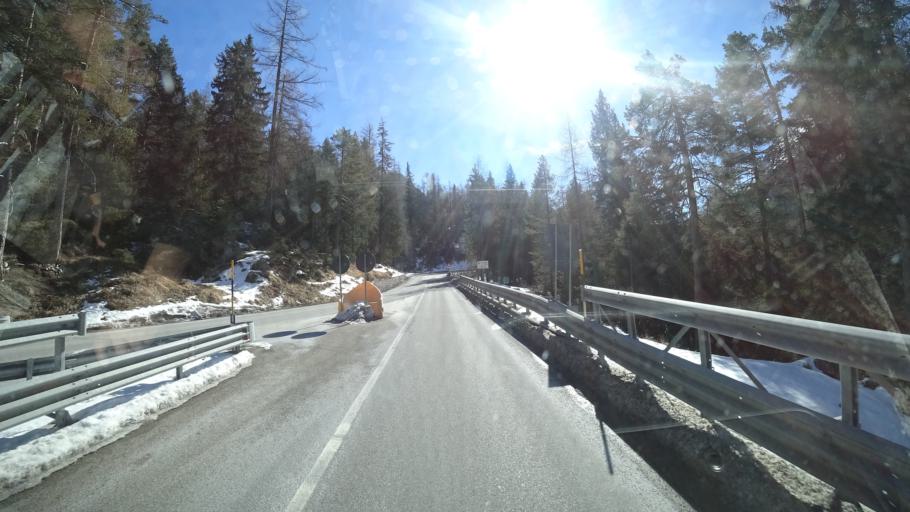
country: IT
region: Veneto
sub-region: Provincia di Belluno
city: Cortina d'Ampezzo
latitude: 46.6021
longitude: 12.1092
